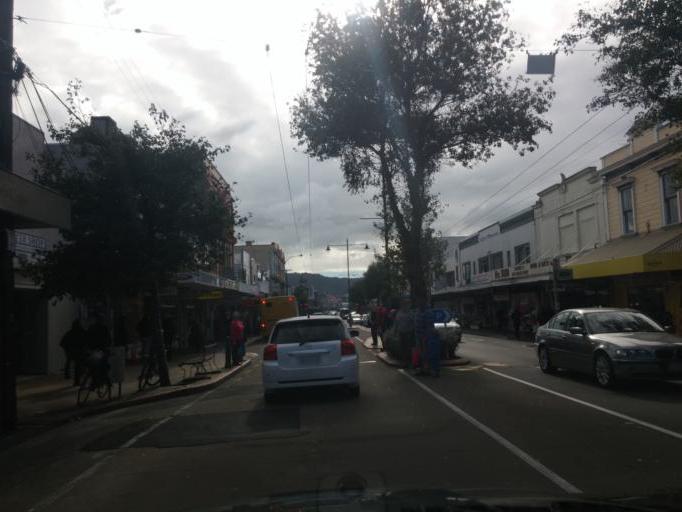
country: NZ
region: Wellington
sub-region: Wellington City
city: Wellington
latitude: -41.3131
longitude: 174.7796
